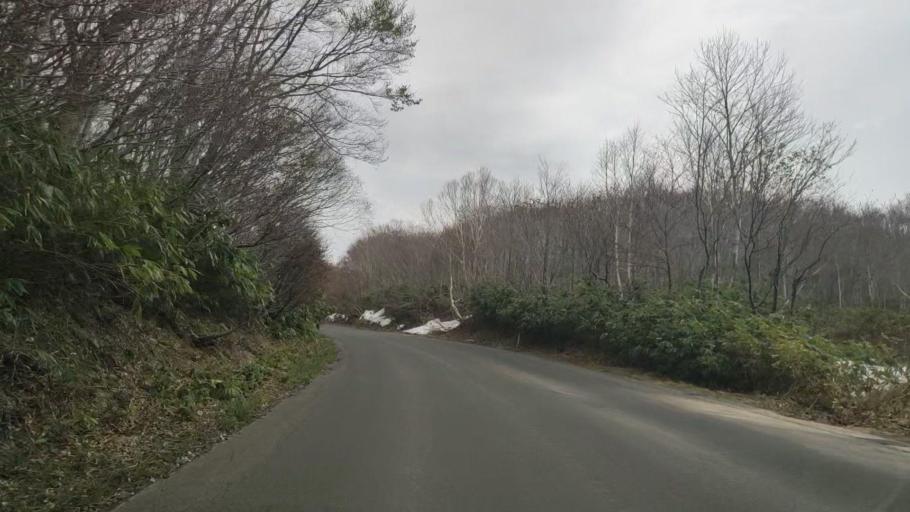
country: JP
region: Aomori
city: Aomori Shi
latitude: 40.6903
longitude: 140.9139
